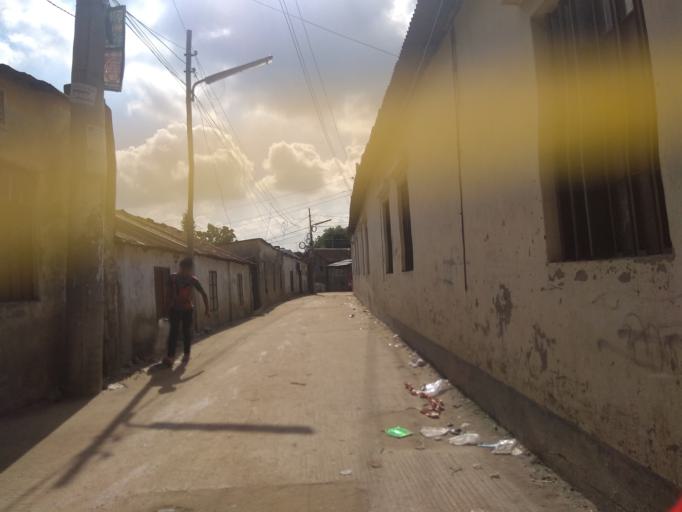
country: BD
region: Dhaka
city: Paltan
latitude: 23.8120
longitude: 90.3892
